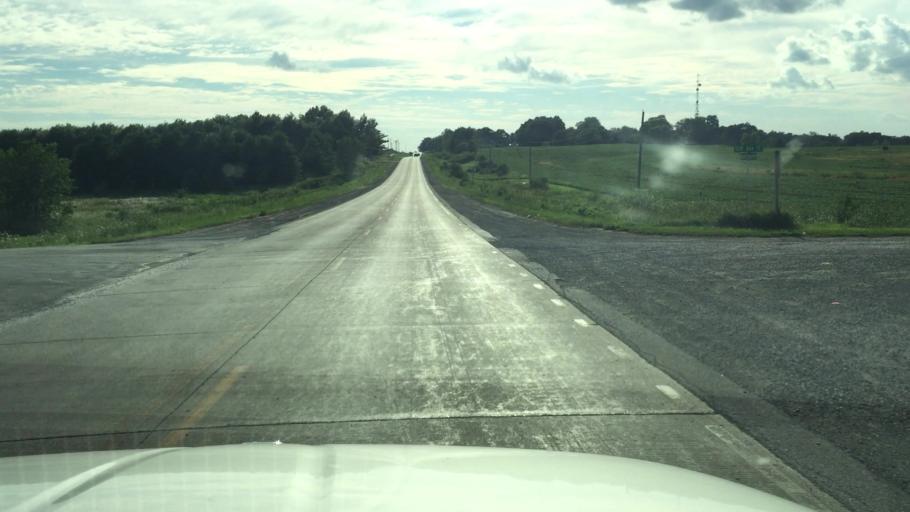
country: US
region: Iowa
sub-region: Johnson County
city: Iowa City
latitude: 41.6710
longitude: -91.4628
